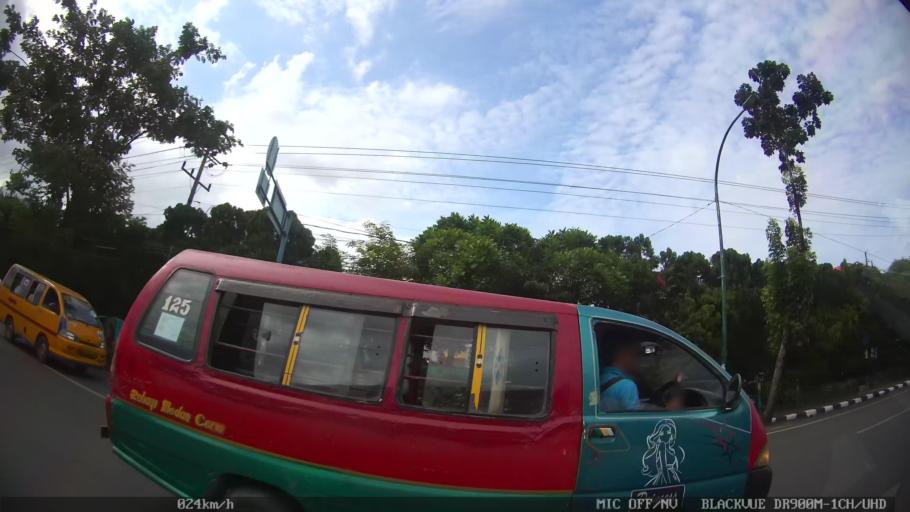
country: ID
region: North Sumatra
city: Medan
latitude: 3.5993
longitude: 98.6840
